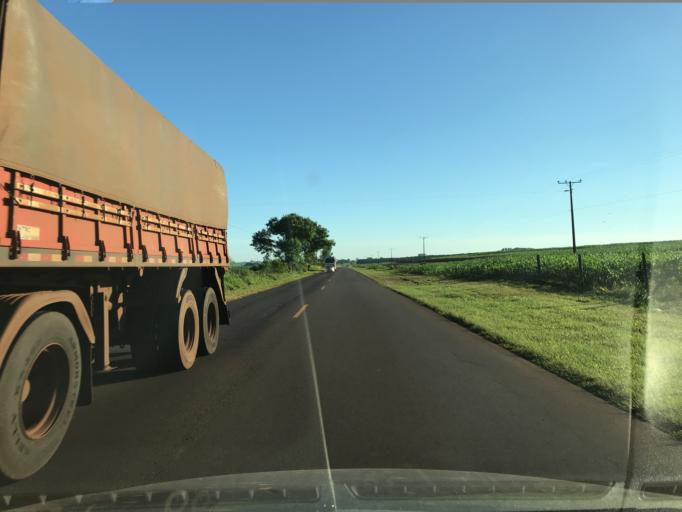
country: BR
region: Parana
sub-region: Palotina
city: Palotina
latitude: -24.1121
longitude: -53.8448
